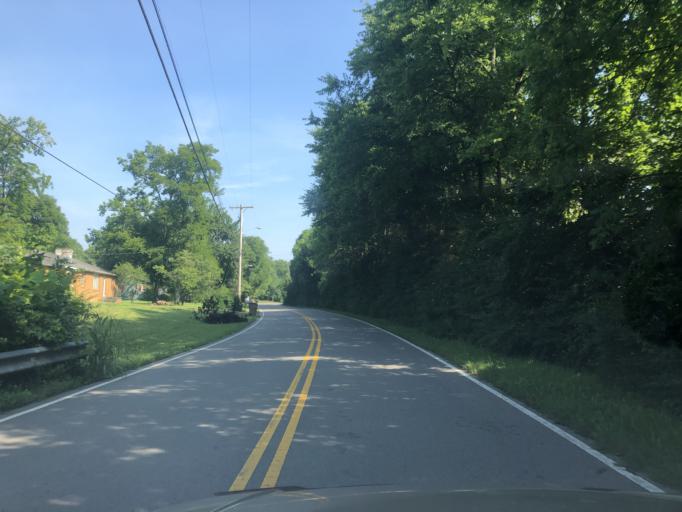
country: US
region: Tennessee
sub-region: Davidson County
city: Lakewood
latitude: 36.2288
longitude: -86.7085
